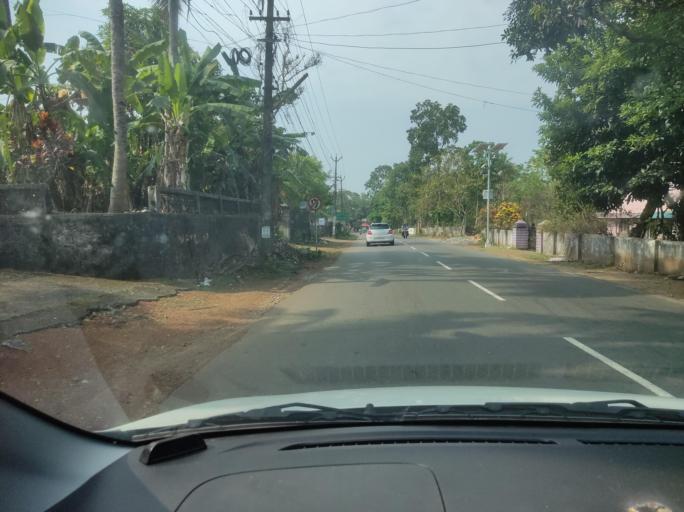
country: IN
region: Kerala
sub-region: Pattanamtitta
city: Adur
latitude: 9.1383
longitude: 76.7295
